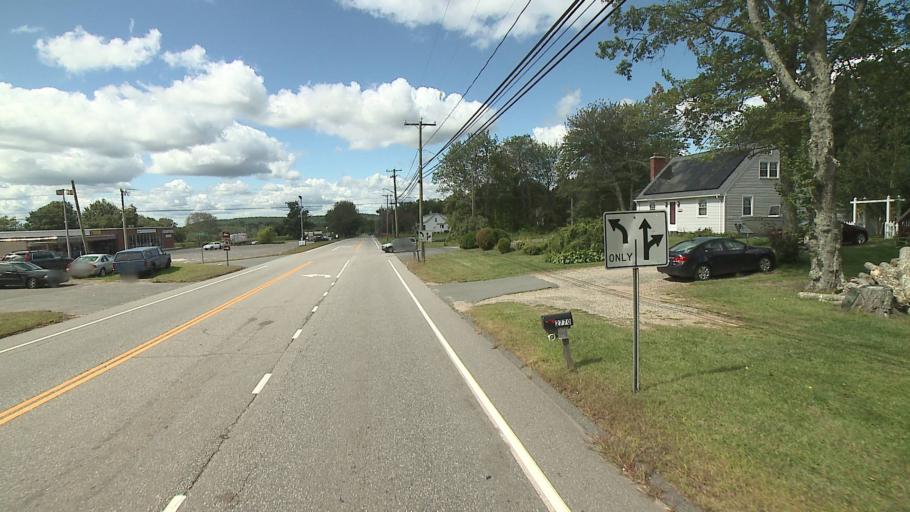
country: US
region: Connecticut
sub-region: Tolland County
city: Rockville
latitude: 41.7966
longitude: -72.4126
